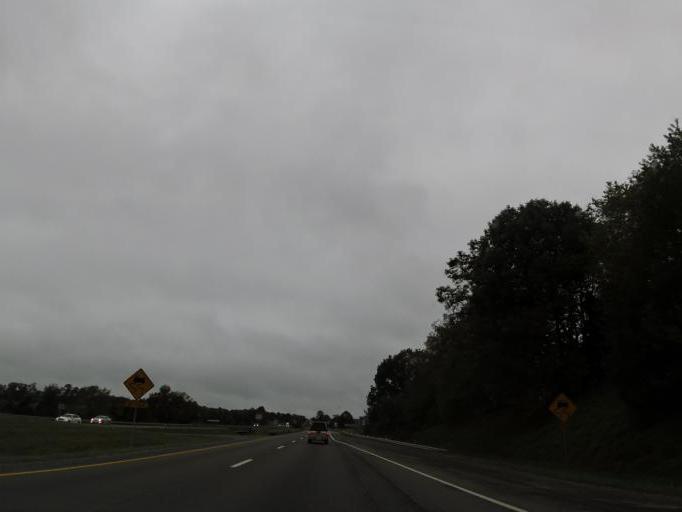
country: US
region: Virginia
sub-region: Wythe County
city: Wytheville
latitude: 36.9634
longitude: -81.0704
